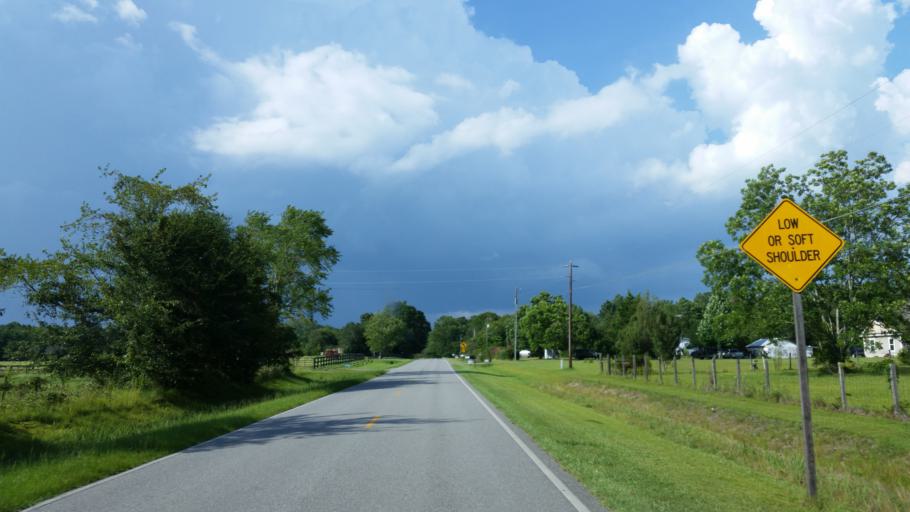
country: US
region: Georgia
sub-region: Lowndes County
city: Hahira
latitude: 30.9705
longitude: -83.3994
